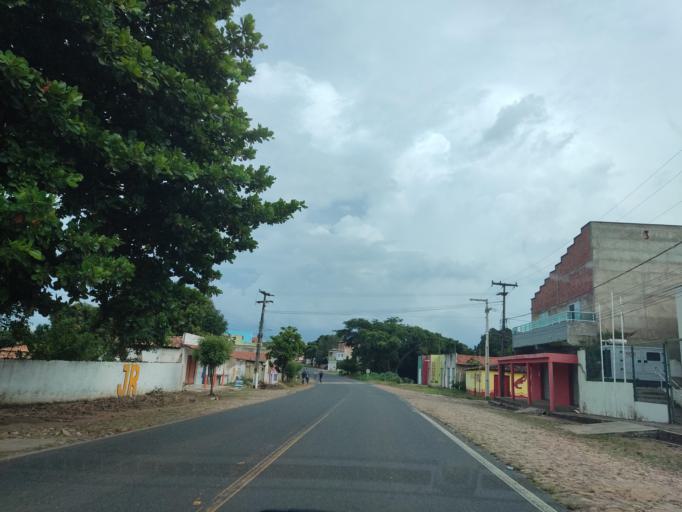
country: BR
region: Piaui
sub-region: Agua Branca
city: Agua Branca
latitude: -5.8200
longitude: -42.5094
